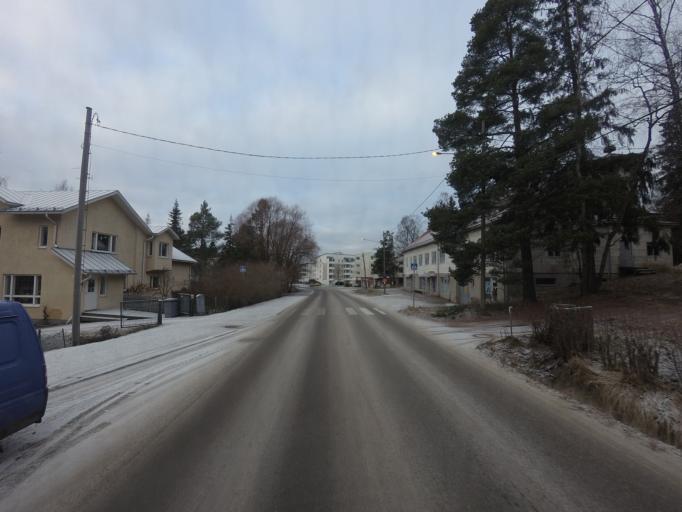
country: FI
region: Uusimaa
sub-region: Helsinki
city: Espoo
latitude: 60.2042
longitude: 24.6859
